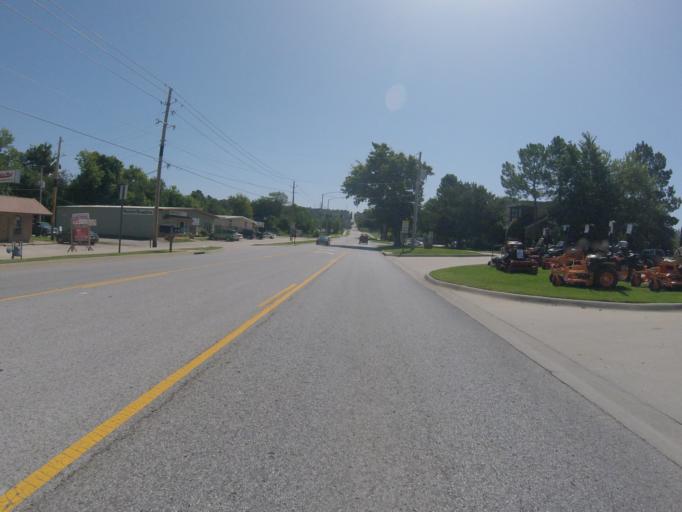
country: US
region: Arkansas
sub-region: Washington County
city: Fayetteville
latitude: 36.0954
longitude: -94.1584
